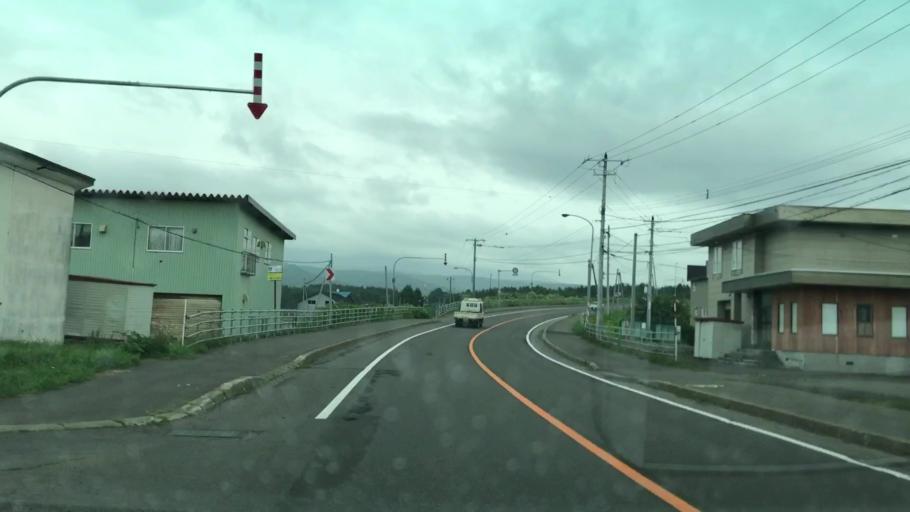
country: JP
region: Hokkaido
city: Niseko Town
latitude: 42.8097
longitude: 140.5338
